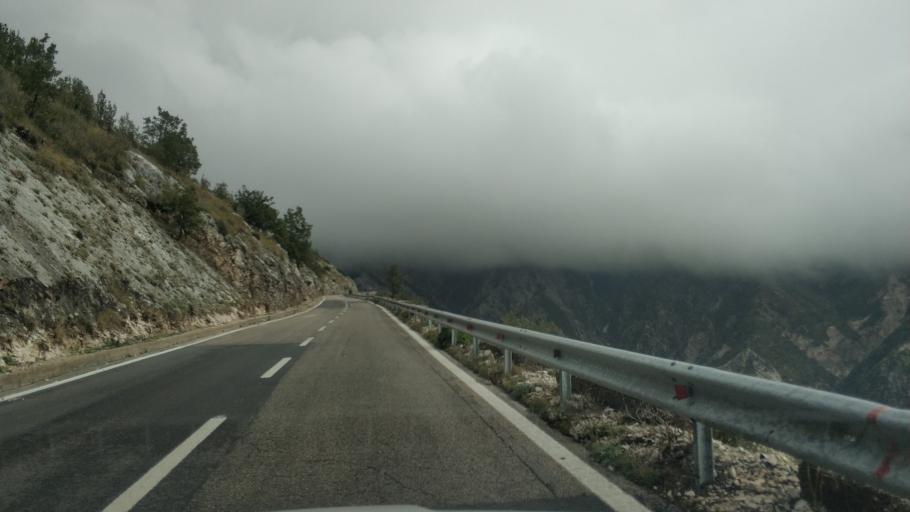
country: AL
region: Vlore
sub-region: Rrethi i Vlores
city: Vranisht
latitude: 40.1895
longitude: 19.6068
